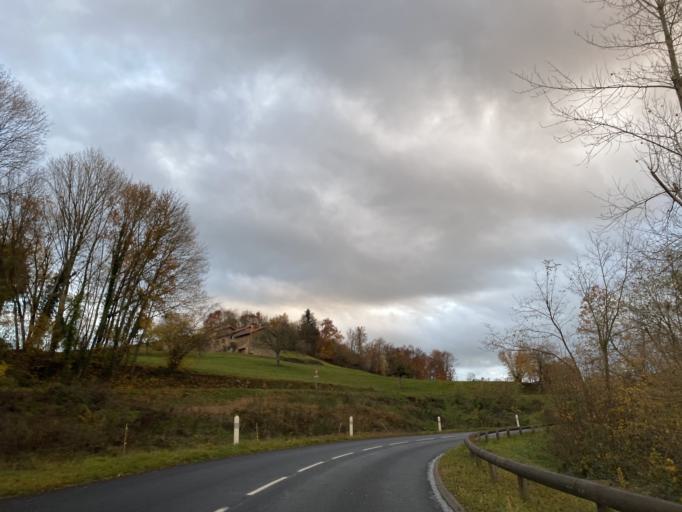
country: FR
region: Auvergne
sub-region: Departement du Puy-de-Dome
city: Cunlhat
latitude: 45.6914
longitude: 3.5787
